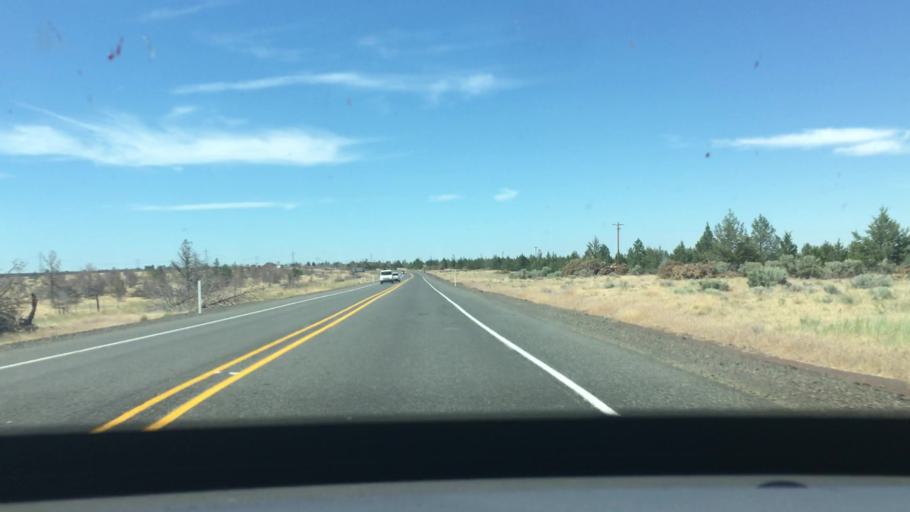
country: US
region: Oregon
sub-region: Jefferson County
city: Madras
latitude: 44.9081
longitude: -120.9394
